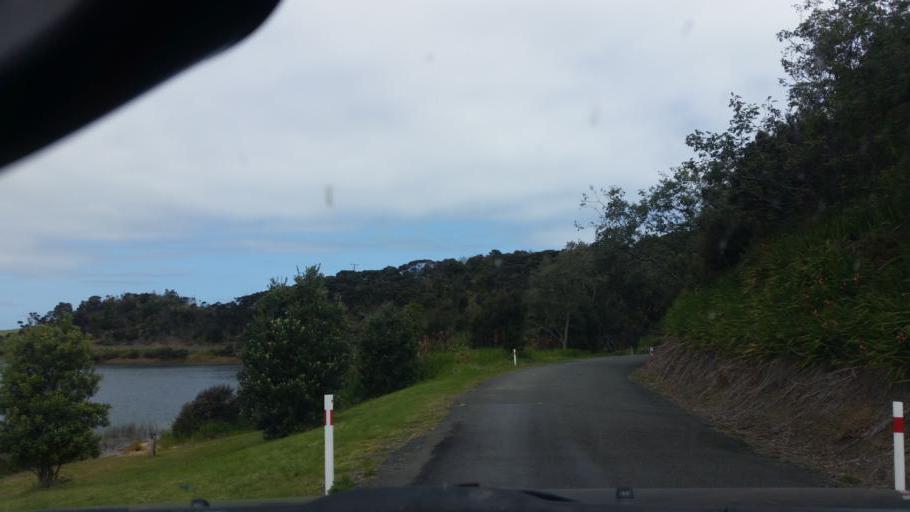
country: NZ
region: Northland
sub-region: Kaipara District
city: Dargaville
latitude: -35.8000
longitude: 173.6278
